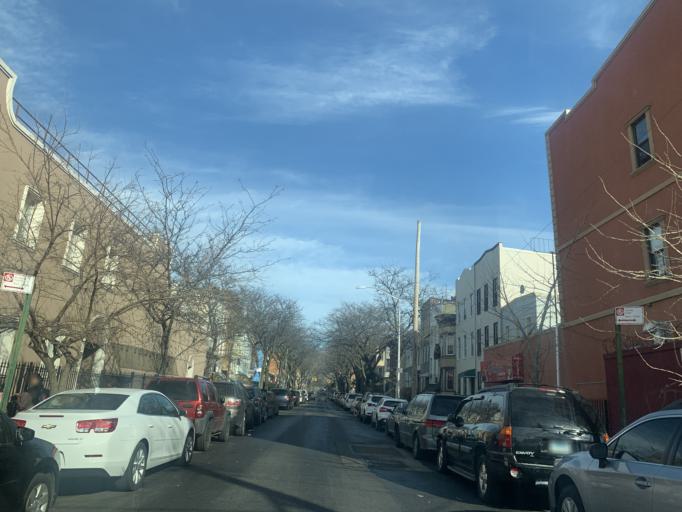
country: US
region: New York
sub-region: Kings County
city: East New York
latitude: 40.7021
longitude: -73.9156
